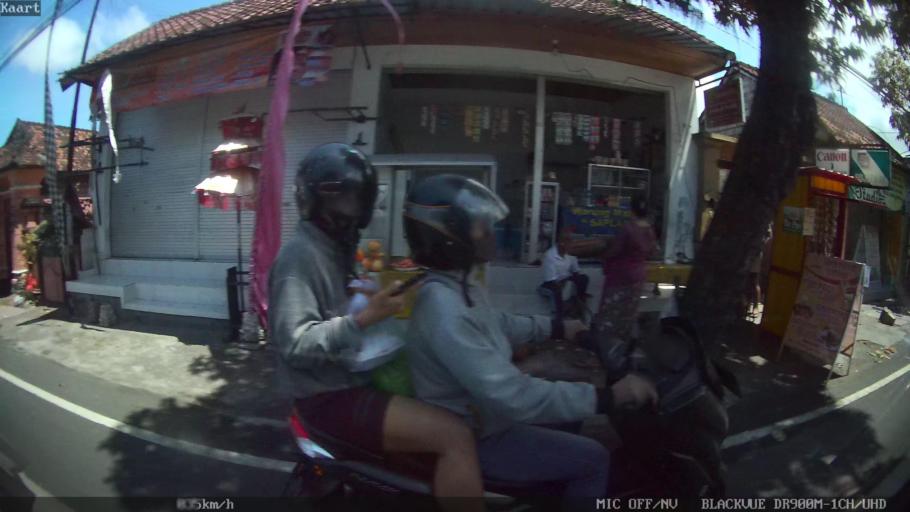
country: ID
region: Bali
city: Banjar Pasekan
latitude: -8.6002
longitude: 115.2829
